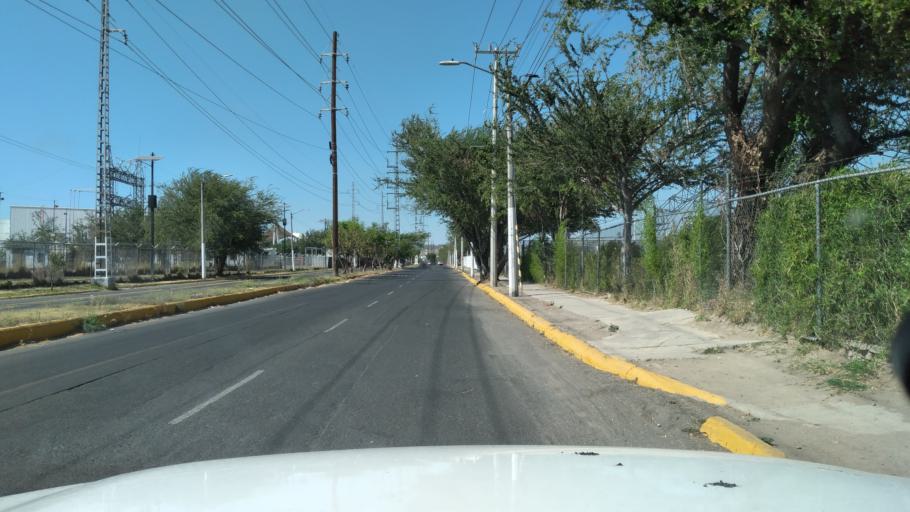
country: MX
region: Jalisco
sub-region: Zapopan
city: Zapopan
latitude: 20.7322
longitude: -103.3767
